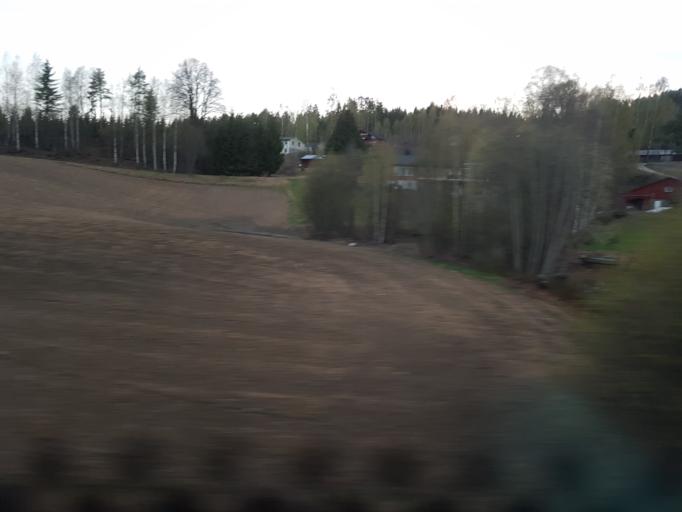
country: NO
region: Hedmark
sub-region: Ringsaker
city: Moelv
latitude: 60.9124
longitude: 10.7277
